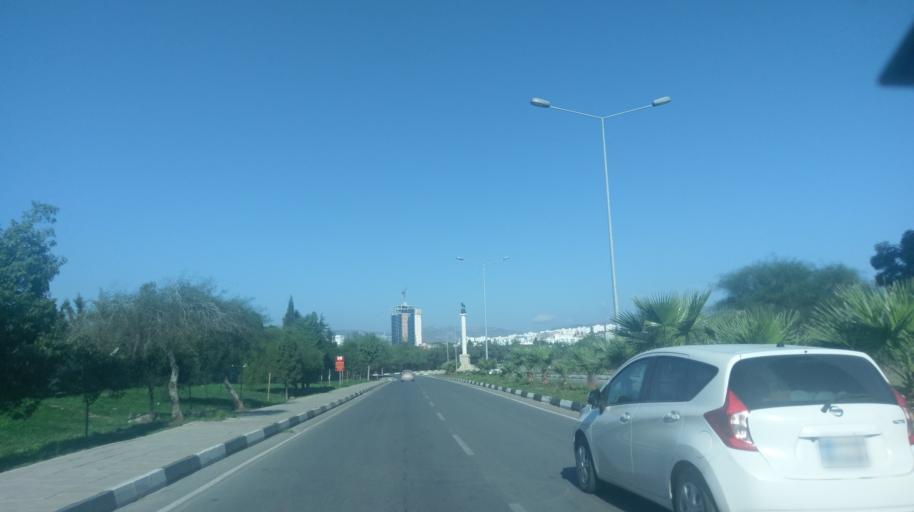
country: CY
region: Lefkosia
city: Nicosia
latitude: 35.2206
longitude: 33.3289
